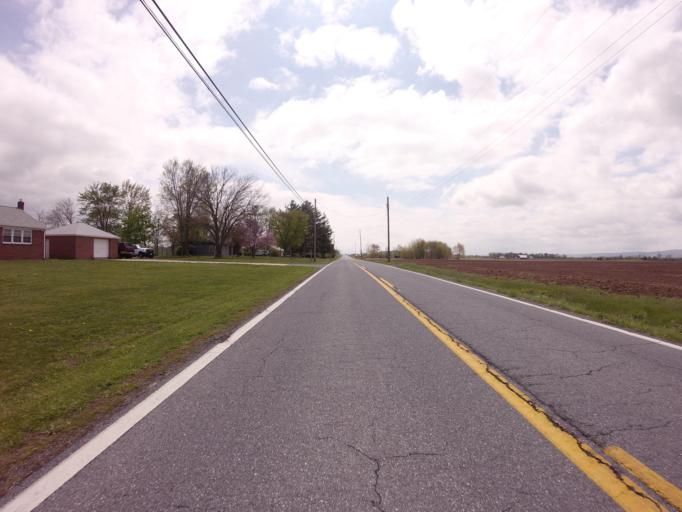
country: US
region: Maryland
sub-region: Frederick County
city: Emmitsburg
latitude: 39.6678
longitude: -77.3377
